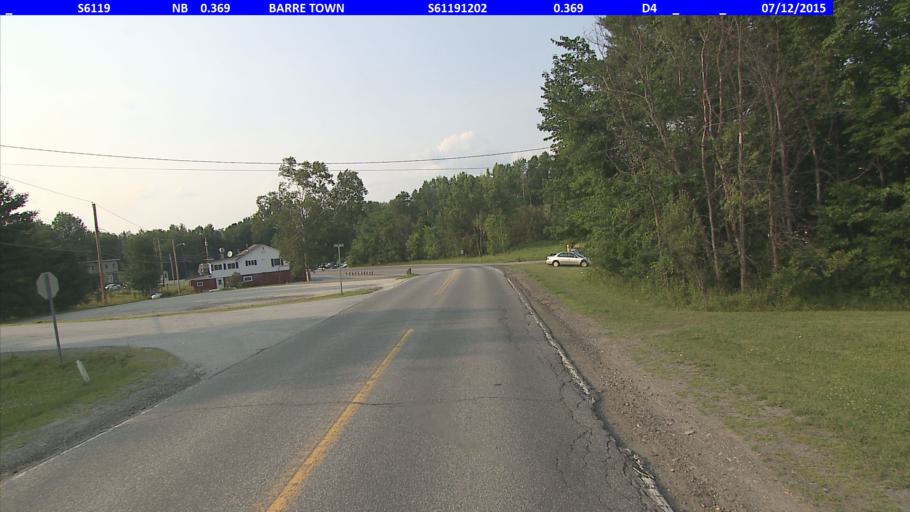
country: US
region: Vermont
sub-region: Washington County
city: South Barre
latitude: 44.1753
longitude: -72.4911
